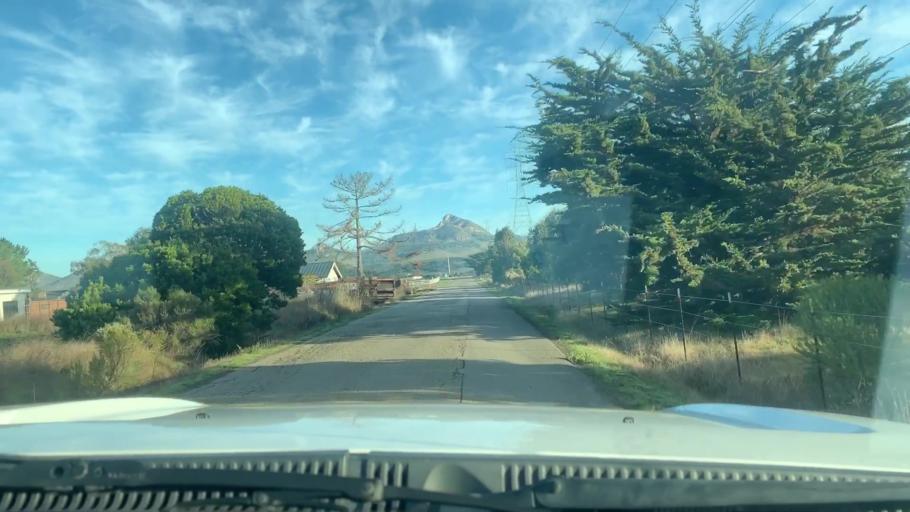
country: US
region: California
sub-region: San Luis Obispo County
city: Los Osos
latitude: 35.2998
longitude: -120.8022
